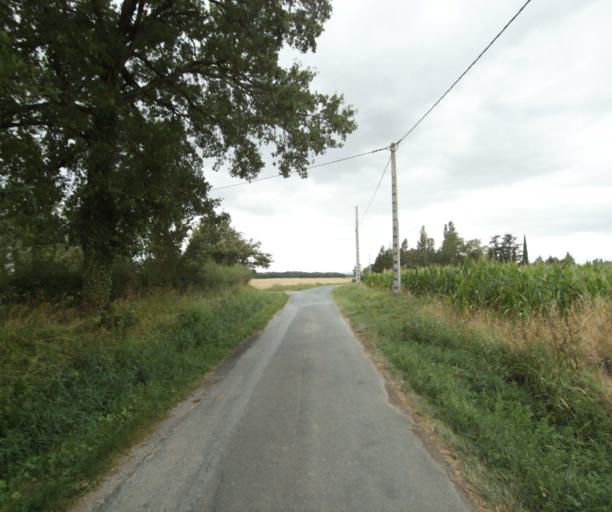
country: FR
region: Midi-Pyrenees
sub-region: Departement du Tarn
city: Soreze
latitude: 43.4610
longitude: 2.0544
